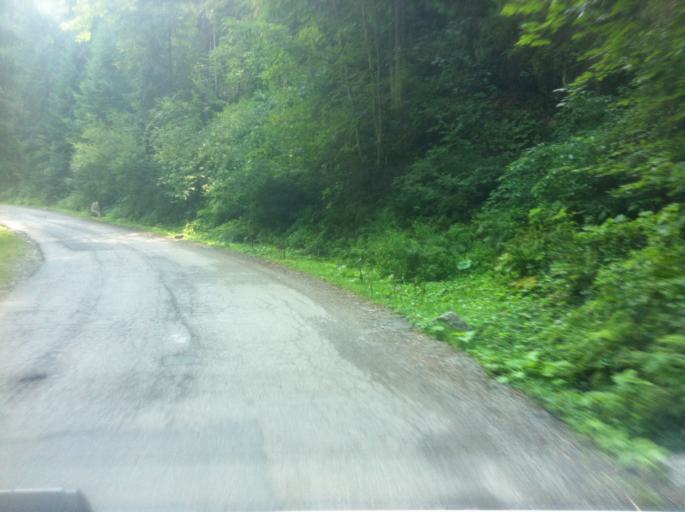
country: RO
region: Hunedoara
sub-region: Oras Petrila
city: Petrila
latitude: 45.4077
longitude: 23.5013
